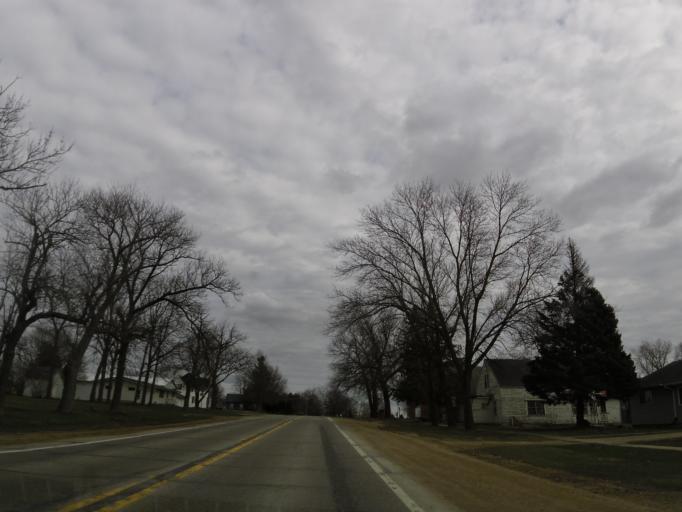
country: US
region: Minnesota
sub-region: Fillmore County
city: Spring Valley
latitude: 43.4900
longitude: -92.3580
